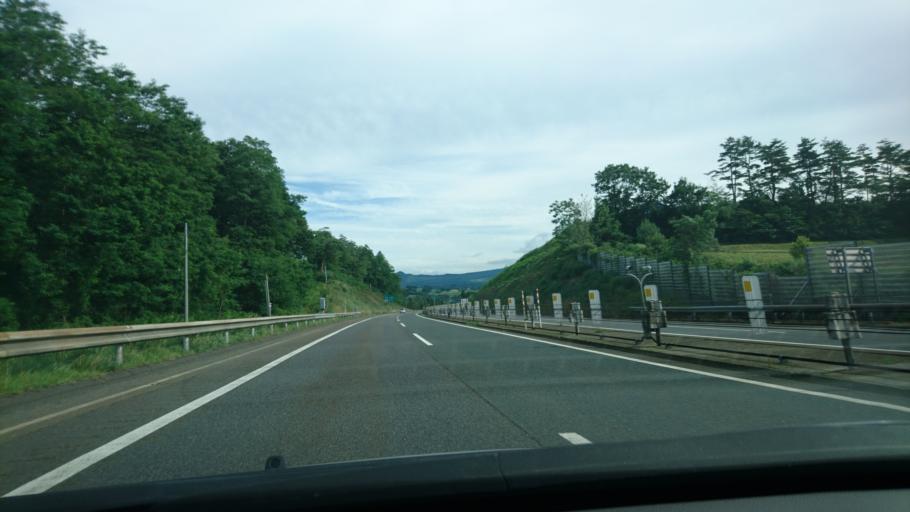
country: JP
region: Iwate
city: Shizukuishi
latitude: 39.9626
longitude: 141.0315
